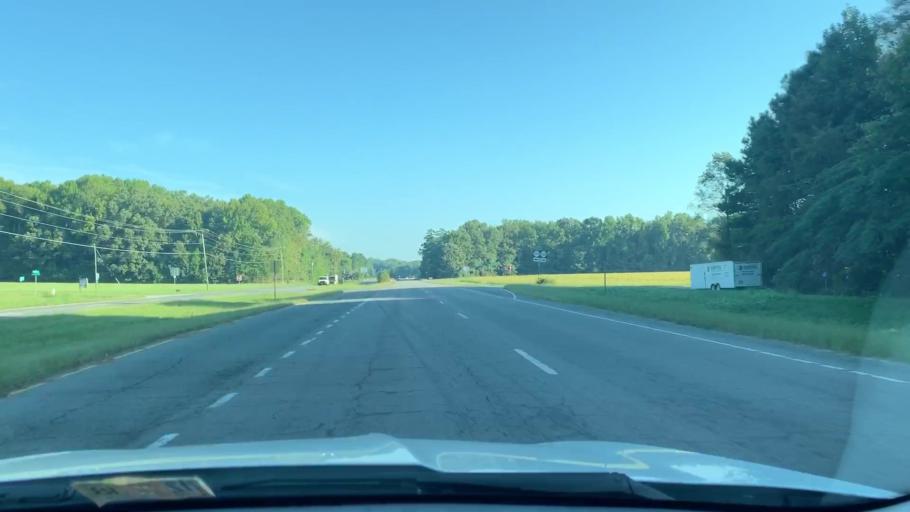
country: US
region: Virginia
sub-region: Lancaster County
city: Kilmarnock
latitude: 37.6871
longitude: -76.3765
